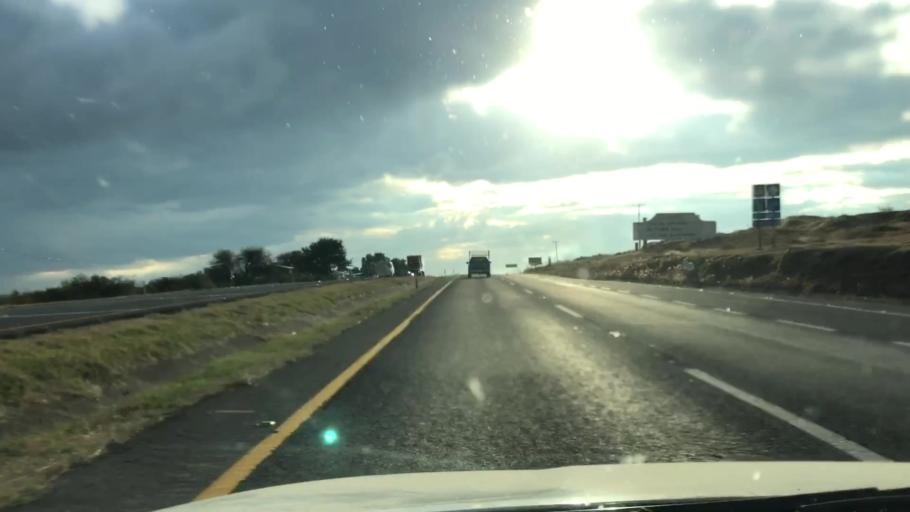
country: MX
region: Guanajuato
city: Penjamo
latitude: 20.3988
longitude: -101.7522
